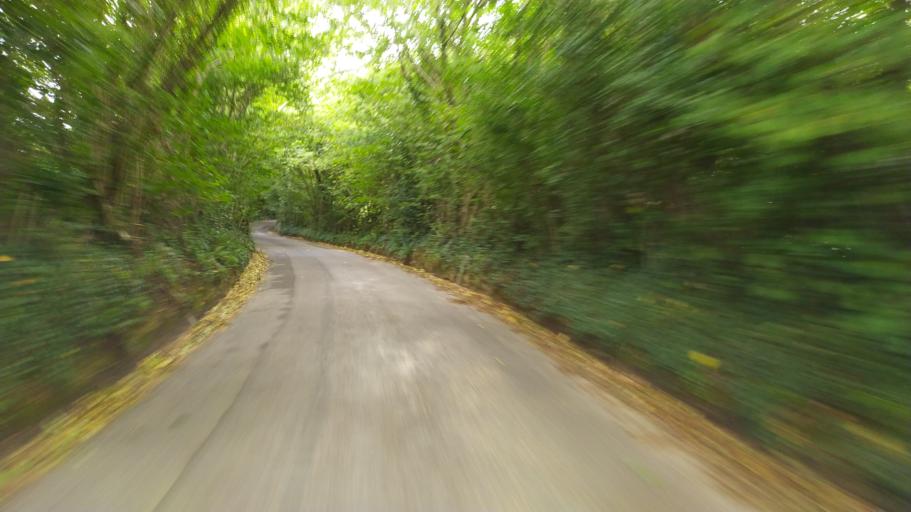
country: GB
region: England
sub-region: Dorset
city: Lytchett Matravers
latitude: 50.7781
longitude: -2.0358
